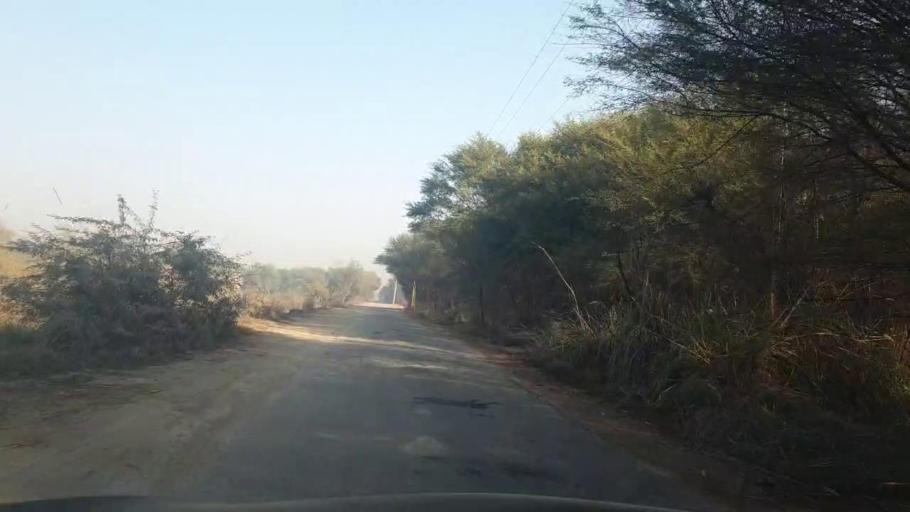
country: PK
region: Sindh
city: Mirpur Mathelo
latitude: 28.0536
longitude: 69.4617
